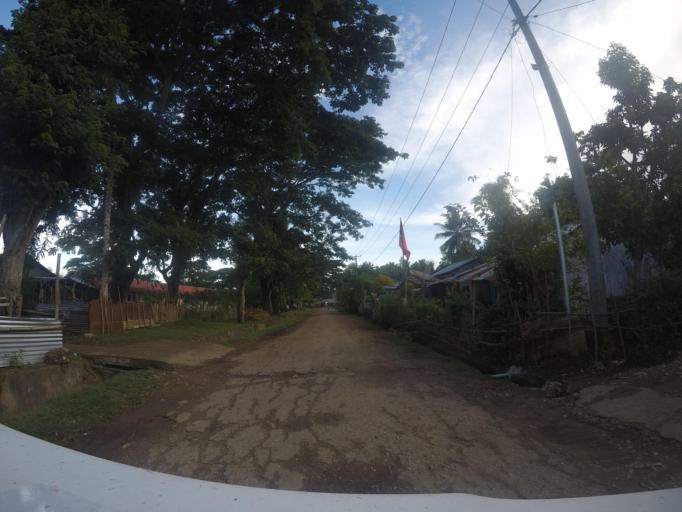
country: TL
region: Lautem
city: Lospalos
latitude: -8.5193
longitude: 126.9967
